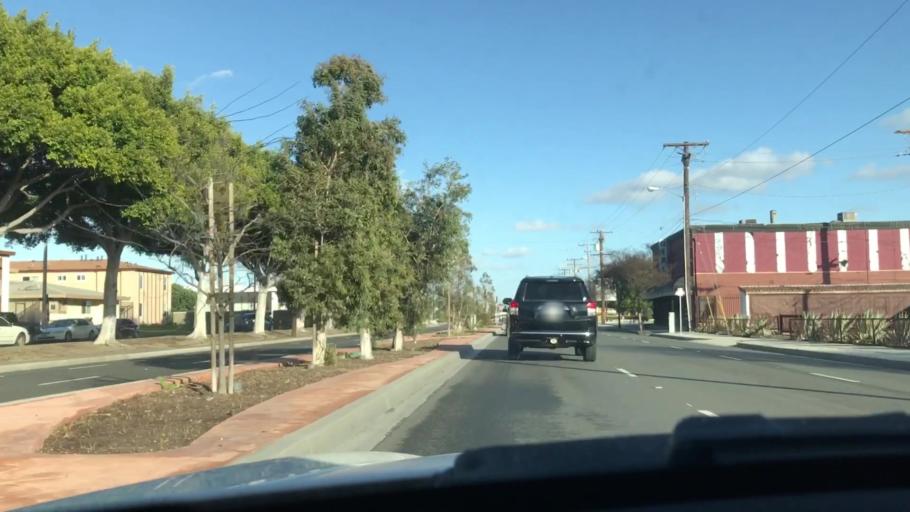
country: US
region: California
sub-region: Los Angeles County
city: Alondra Park
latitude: 33.9019
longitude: -118.3229
